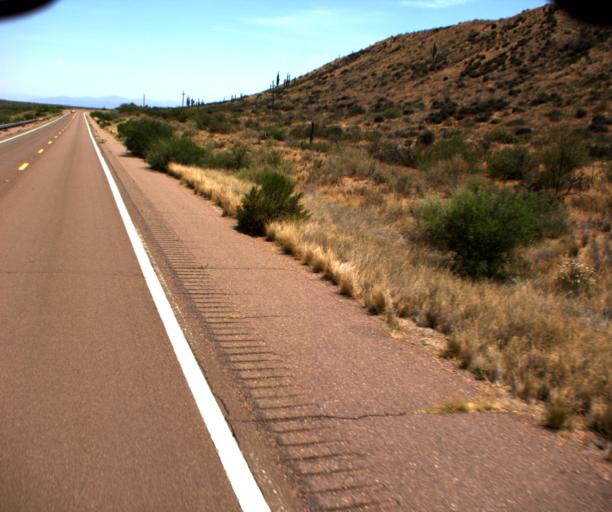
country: US
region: Arizona
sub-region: Gila County
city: Tonto Basin
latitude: 33.9122
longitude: -111.3126
